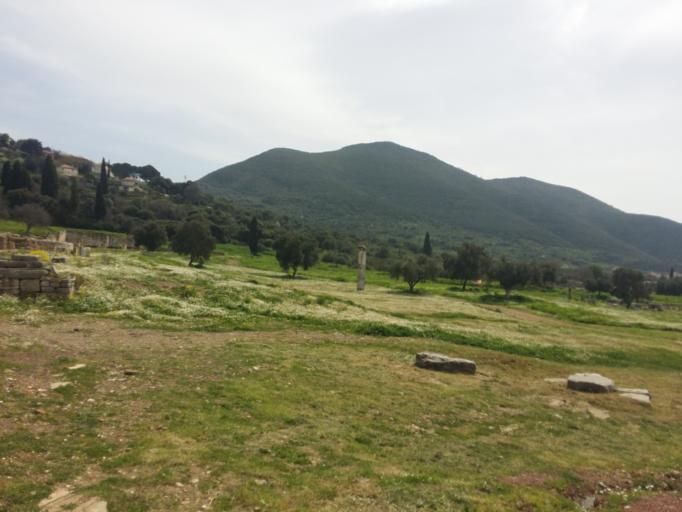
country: GR
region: Peloponnese
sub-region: Nomos Messinias
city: Meligalas
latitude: 37.1779
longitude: 21.9195
